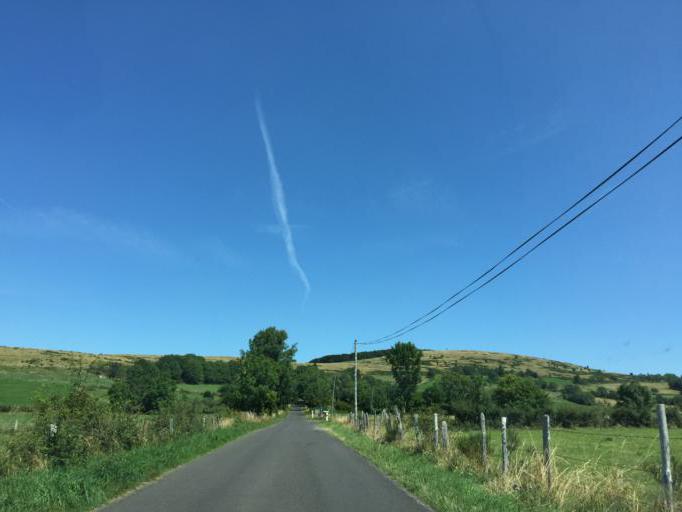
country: FR
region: Midi-Pyrenees
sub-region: Departement de l'Aveyron
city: Laguiole
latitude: 44.6530
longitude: 2.8882
